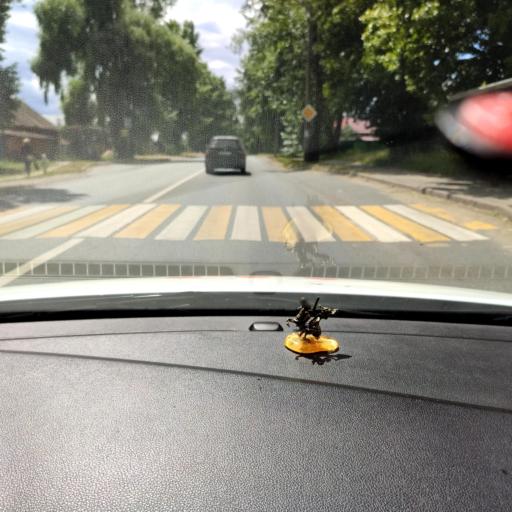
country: RU
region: Tatarstan
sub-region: Gorod Kazan'
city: Kazan
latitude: 55.7029
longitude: 49.1442
